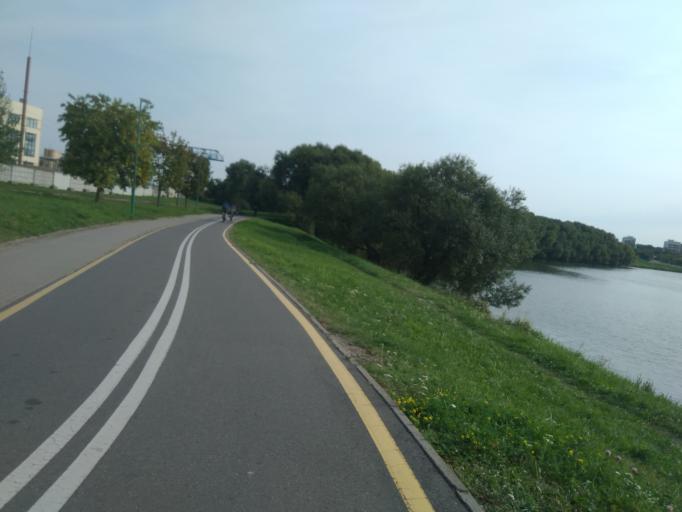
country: BY
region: Minsk
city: Minsk
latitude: 53.8820
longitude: 27.5748
